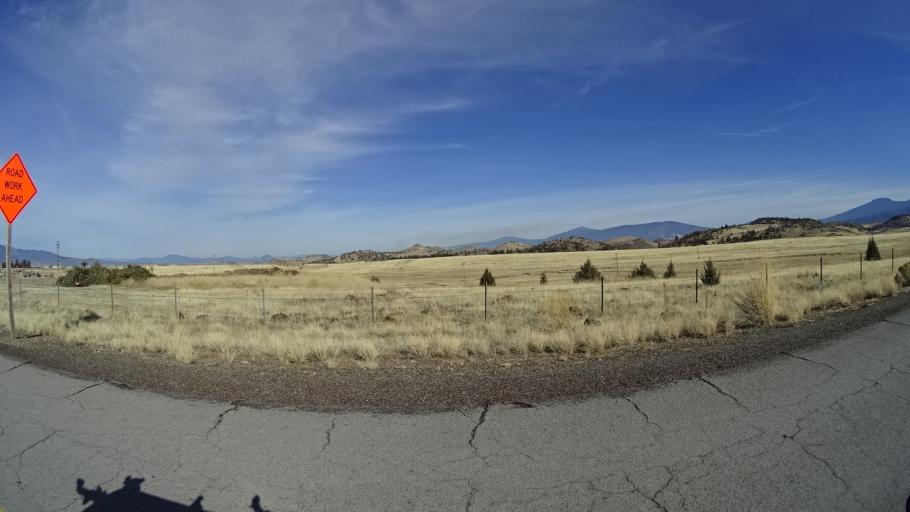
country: US
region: California
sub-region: Siskiyou County
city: Weed
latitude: 41.4720
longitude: -122.4485
